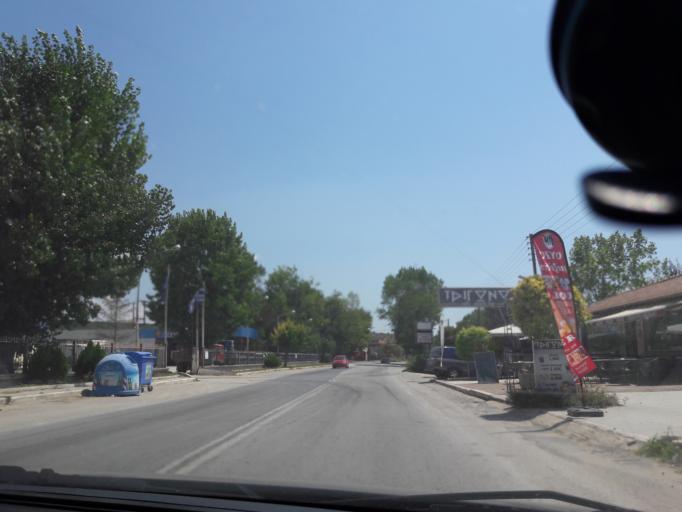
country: GR
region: Central Macedonia
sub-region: Nomos Chalkidikis
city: Nea Kallikrateia
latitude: 40.3389
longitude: 23.0629
